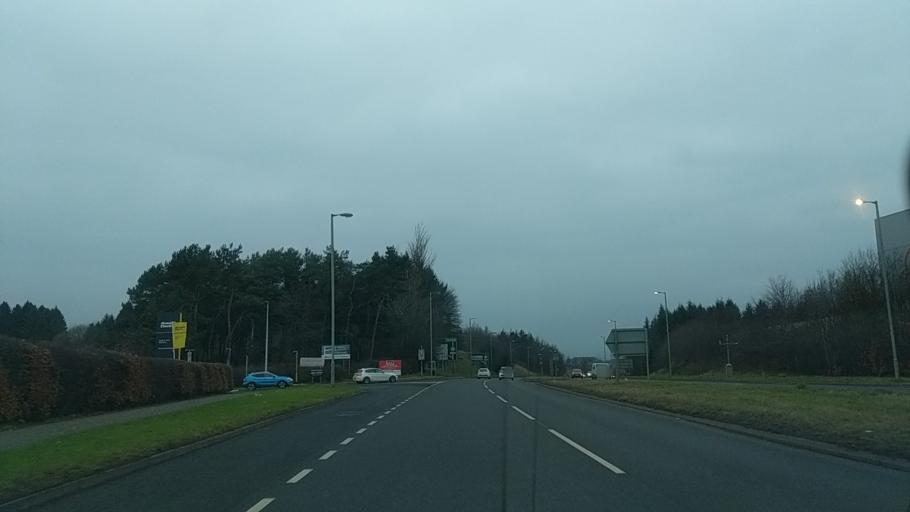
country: GB
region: Scotland
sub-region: Glasgow City
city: Carmunnock
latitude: 55.7669
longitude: -4.2177
